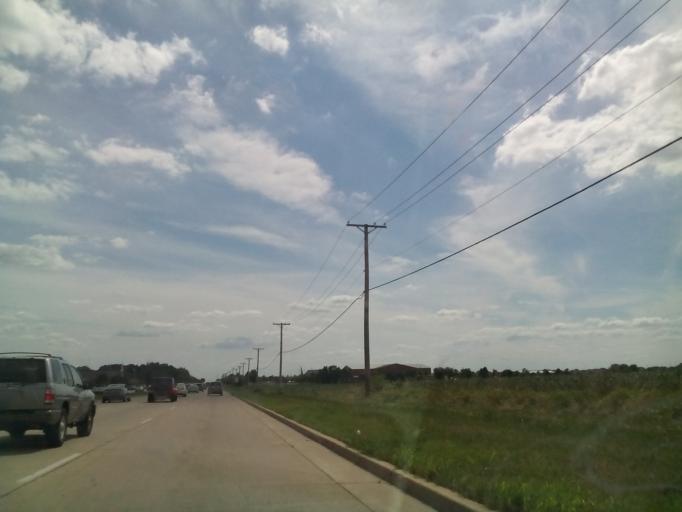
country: US
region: Illinois
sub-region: DuPage County
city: Naperville
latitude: 41.7434
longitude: -88.2062
